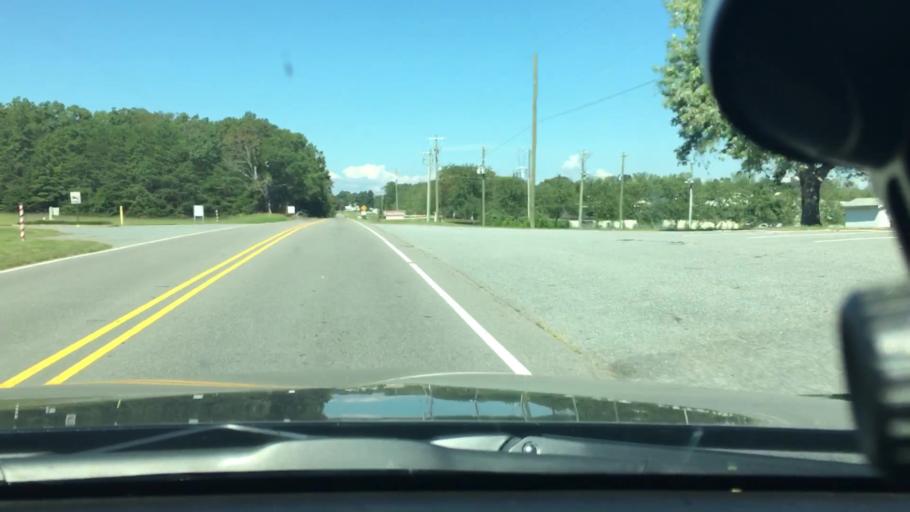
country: US
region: North Carolina
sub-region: Rutherford County
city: Spindale
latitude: 35.3161
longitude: -81.9290
